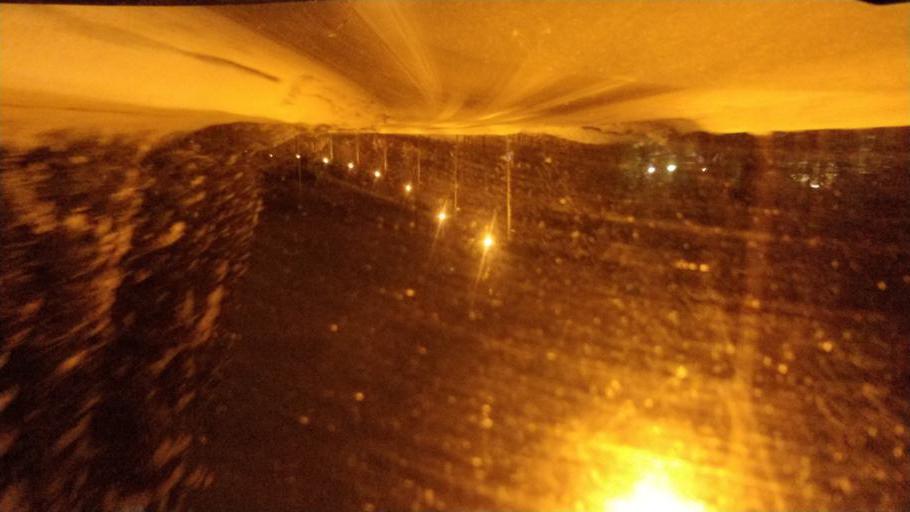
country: FI
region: Lapland
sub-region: Rovaniemi
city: Rovaniemi
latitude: 66.3767
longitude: 25.3829
